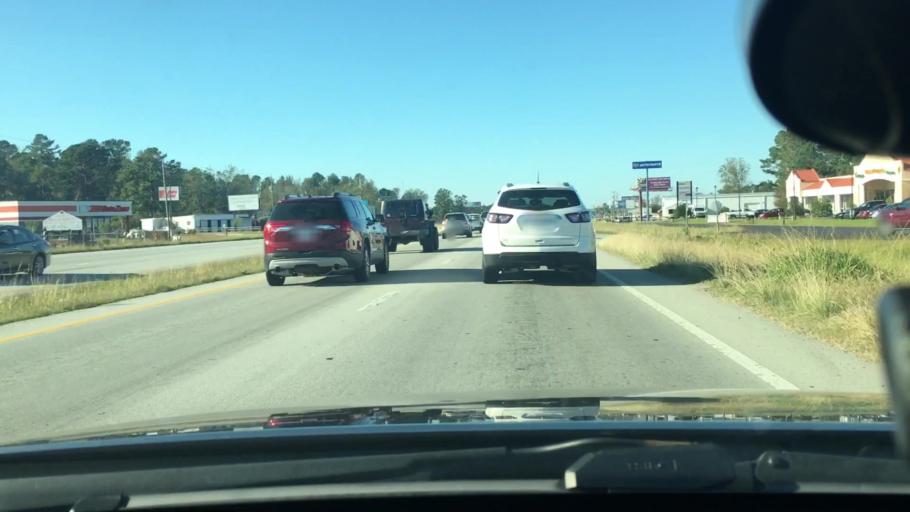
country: US
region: North Carolina
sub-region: Craven County
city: James City
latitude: 35.0760
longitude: -77.0285
